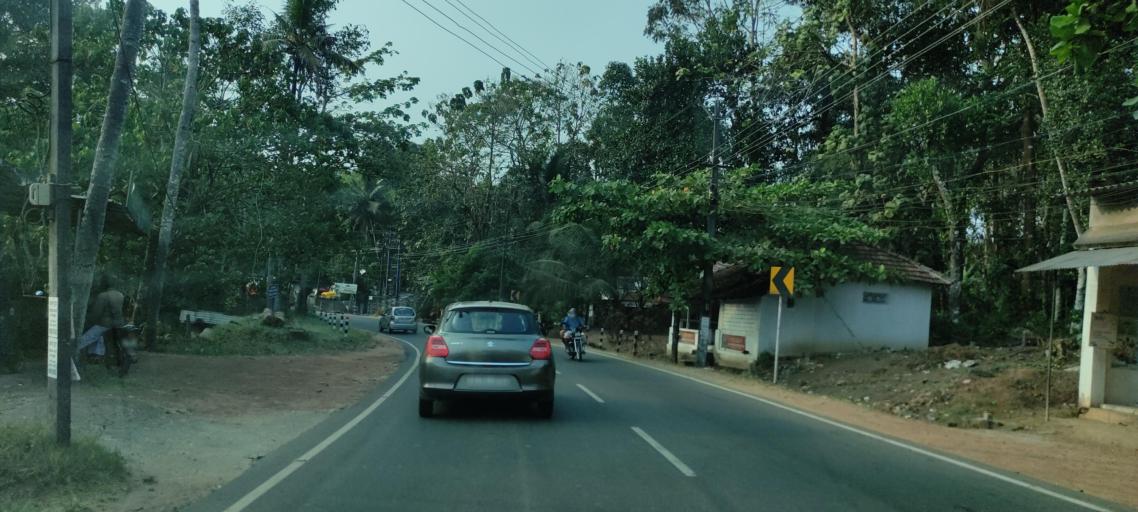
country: IN
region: Kerala
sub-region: Pattanamtitta
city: Adur
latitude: 9.1702
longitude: 76.6545
